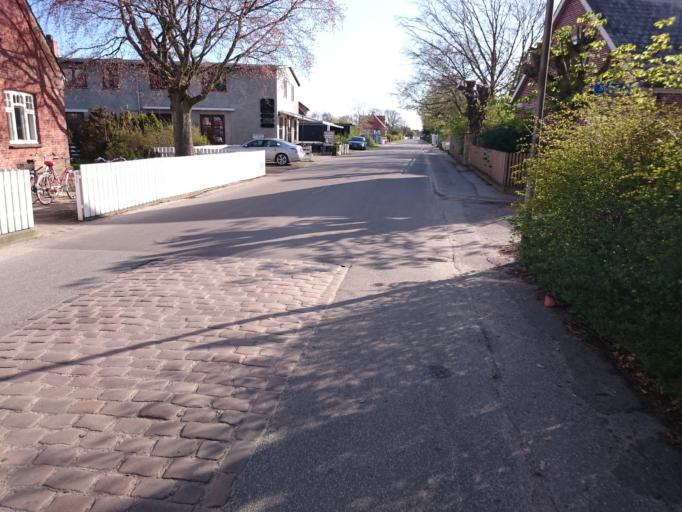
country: DK
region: South Denmark
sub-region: Fano Kommune
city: Nordby
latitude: 55.4433
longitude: 8.4018
